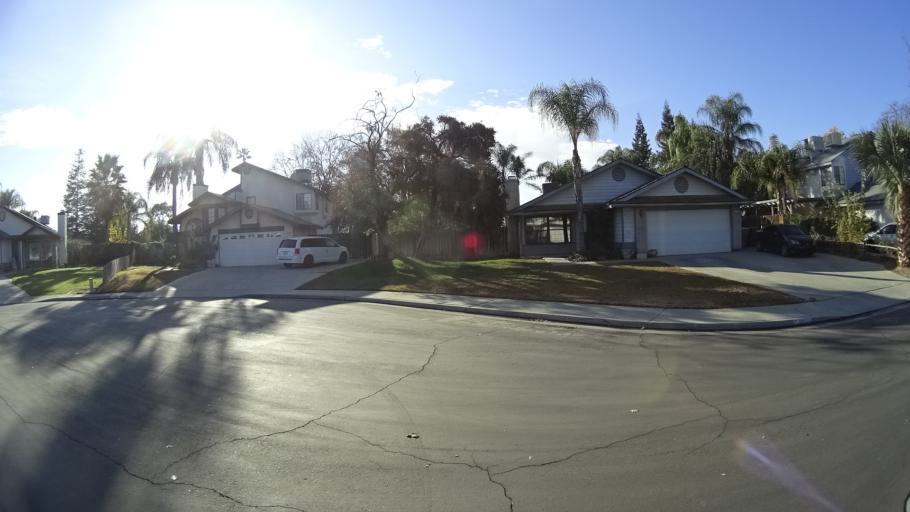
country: US
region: California
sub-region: Kern County
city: Rosedale
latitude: 35.3487
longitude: -119.1484
